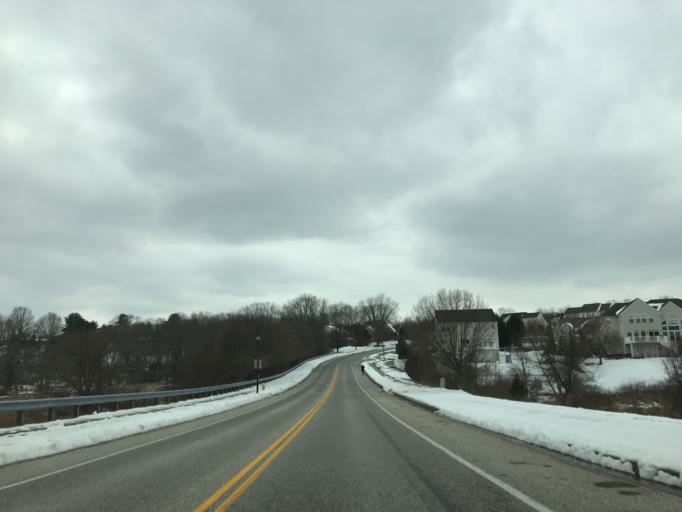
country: US
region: Maryland
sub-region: Harford County
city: Bel Air North
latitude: 39.5619
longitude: -76.3911
